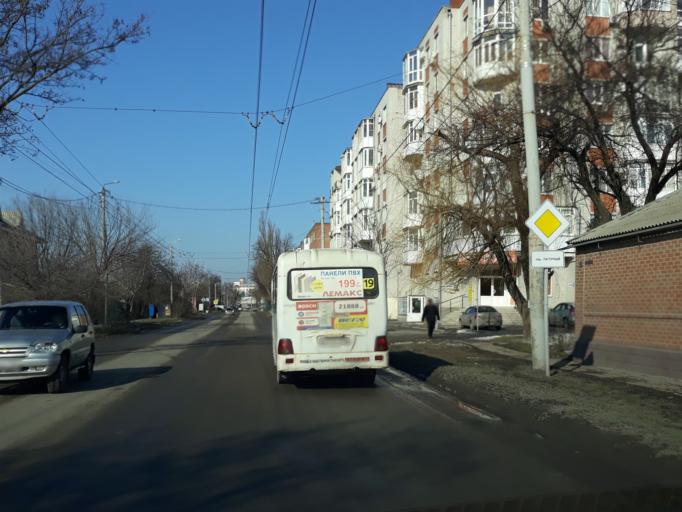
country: RU
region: Rostov
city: Taganrog
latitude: 47.2031
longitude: 38.9020
